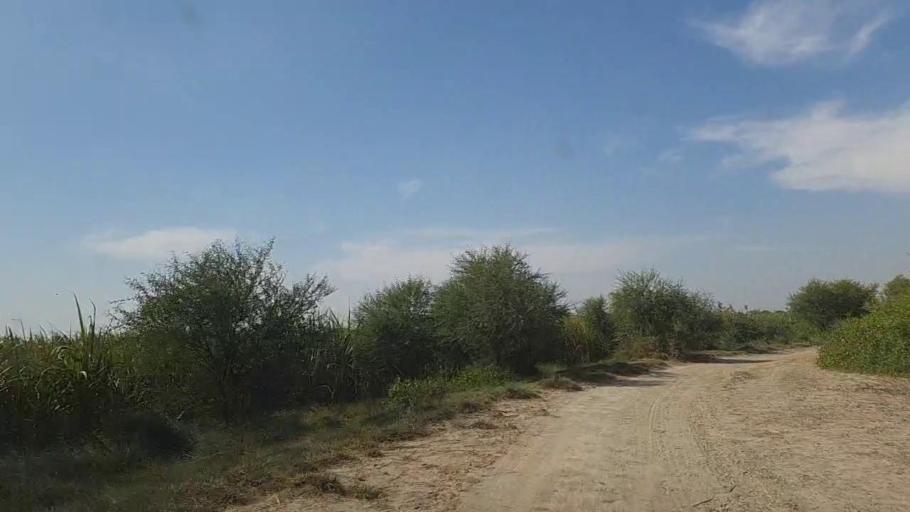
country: PK
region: Sindh
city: Mirpur Batoro
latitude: 24.8092
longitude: 68.2654
